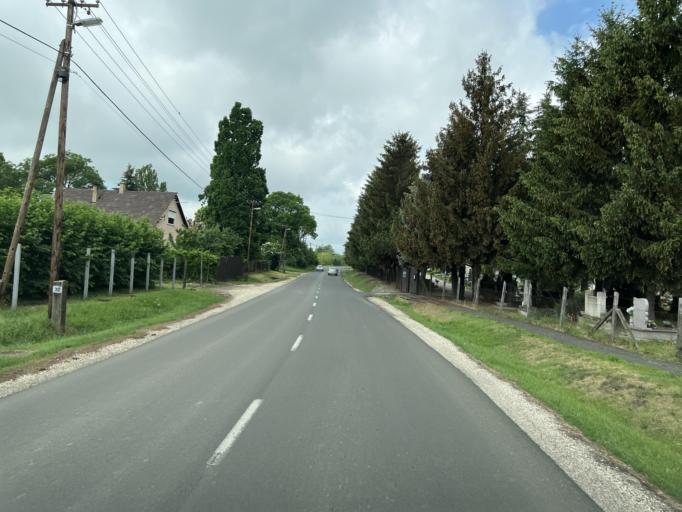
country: HU
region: Pest
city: Kartal
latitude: 47.7242
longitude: 19.5418
